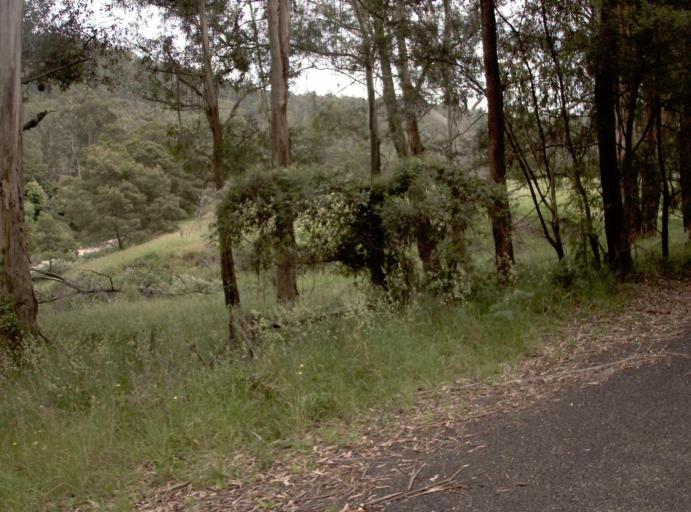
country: AU
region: New South Wales
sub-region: Bombala
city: Bombala
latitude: -37.4454
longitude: 149.1939
